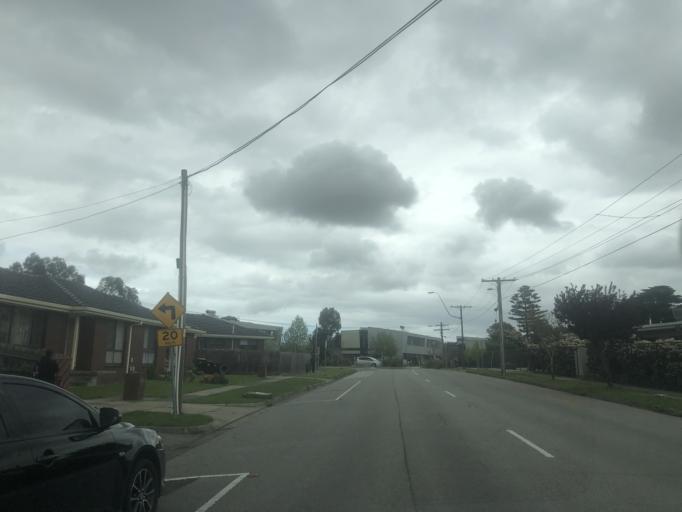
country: AU
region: Victoria
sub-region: Greater Dandenong
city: Dandenong North
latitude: -37.9791
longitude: 145.2137
